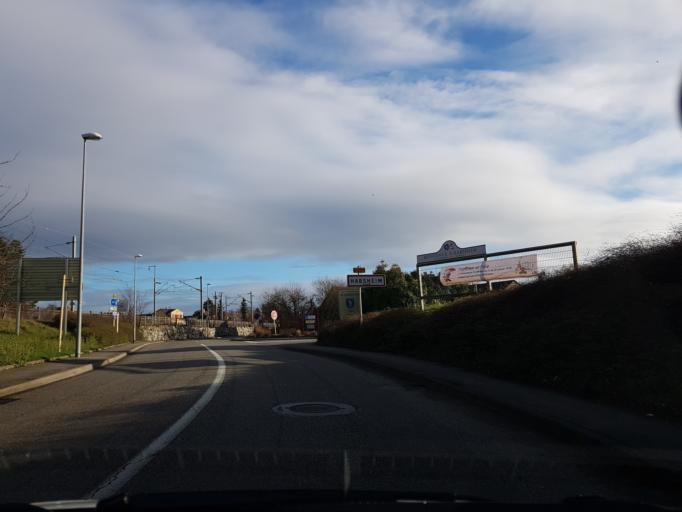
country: FR
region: Alsace
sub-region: Departement du Haut-Rhin
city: Habsheim
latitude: 47.7395
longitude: 7.4162
